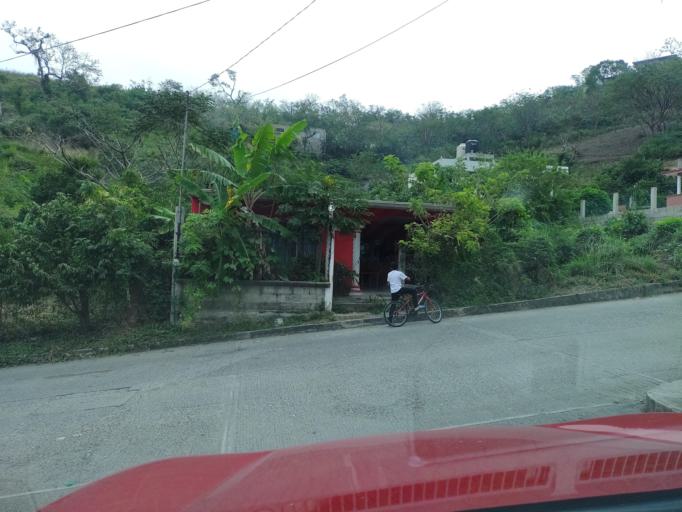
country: MX
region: Veracruz
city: Papantla de Olarte
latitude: 20.4589
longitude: -97.3303
